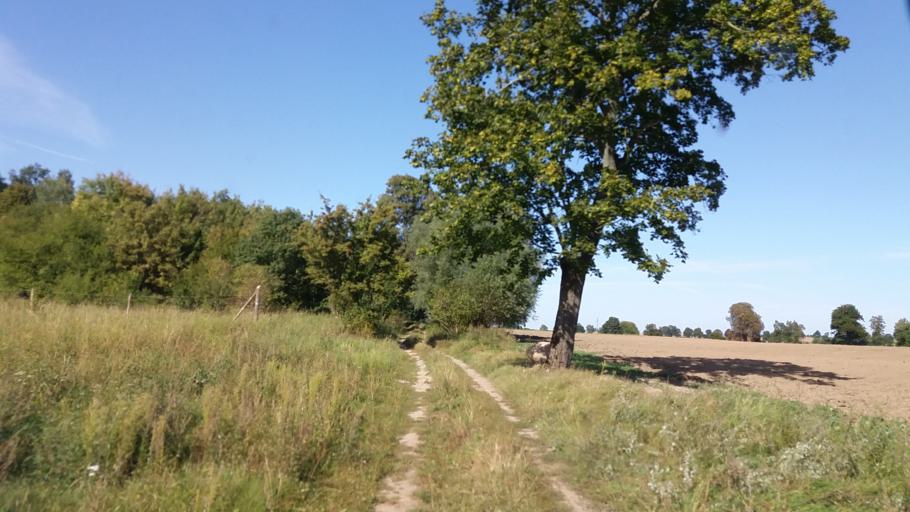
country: PL
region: West Pomeranian Voivodeship
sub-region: Powiat choszczenski
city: Krzecin
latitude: 53.1328
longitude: 15.5033
